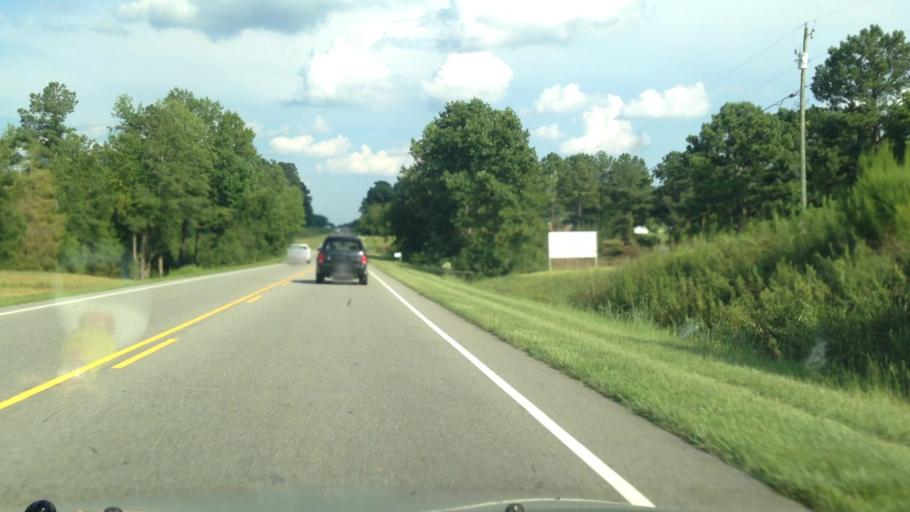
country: US
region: North Carolina
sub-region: Harnett County
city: Lillington
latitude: 35.4173
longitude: -78.8759
